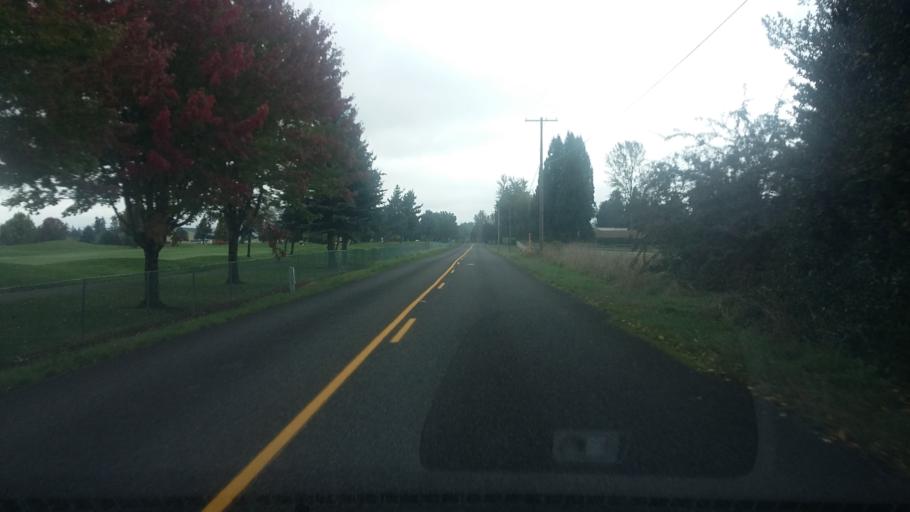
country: US
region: Washington
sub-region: Clark County
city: La Center
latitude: 45.8317
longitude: -122.6825
